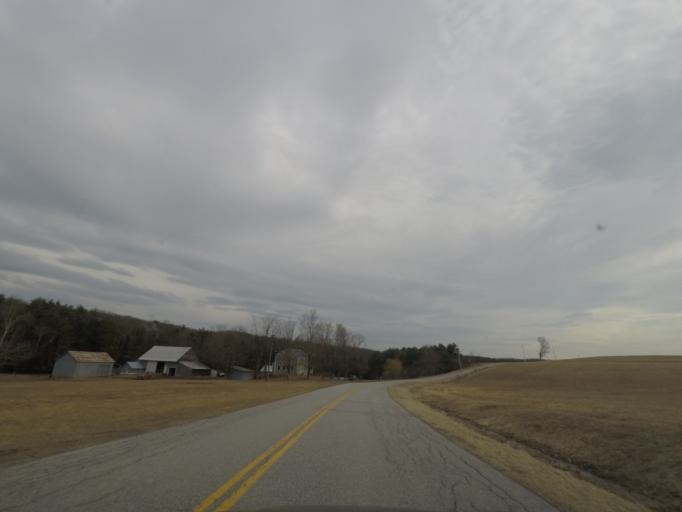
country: US
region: New York
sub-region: Rensselaer County
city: Hoosick Falls
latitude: 42.8843
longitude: -73.4420
